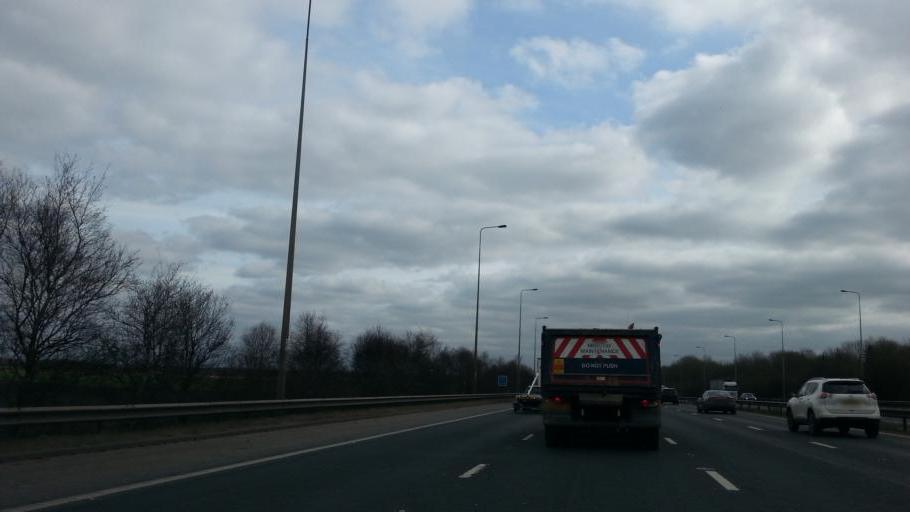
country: GB
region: England
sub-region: Warrington
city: Croft
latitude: 53.4105
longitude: -2.5311
